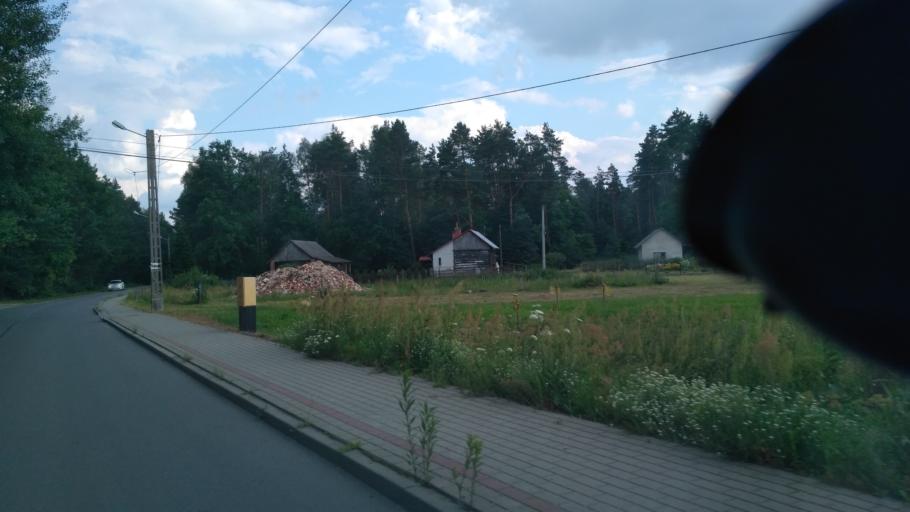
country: PL
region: Subcarpathian Voivodeship
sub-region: Powiat rzeszowski
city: Wysoka Glogowska
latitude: 50.1339
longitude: 22.0215
